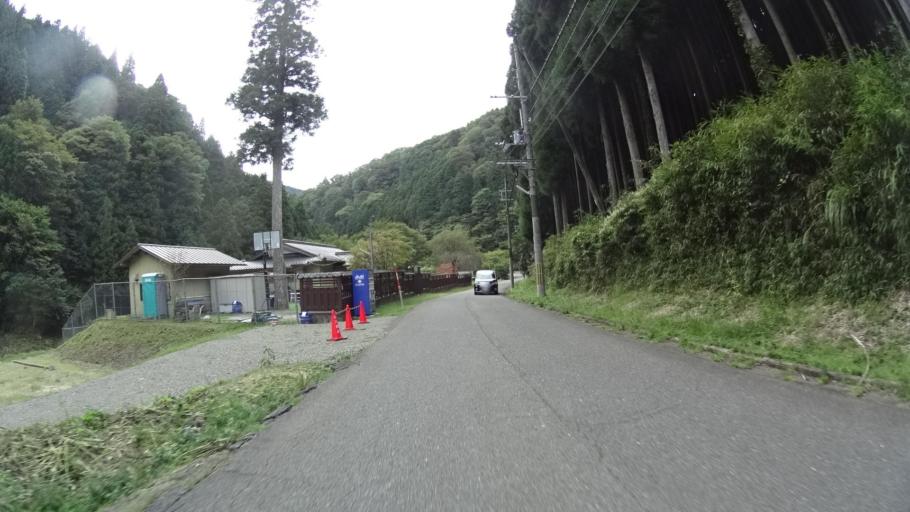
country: JP
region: Shiga Prefecture
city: Kitahama
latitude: 35.2074
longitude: 135.7517
